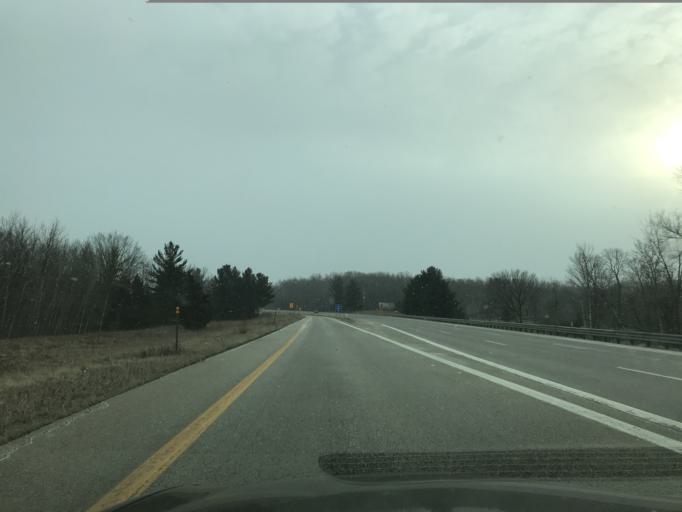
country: US
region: Michigan
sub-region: Clare County
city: Clare
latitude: 43.8543
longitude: -84.7789
